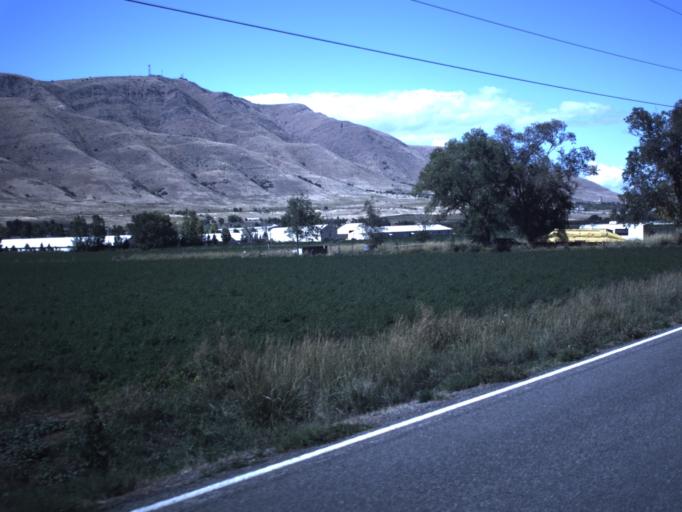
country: US
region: Utah
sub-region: Utah County
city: West Mountain
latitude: 40.0664
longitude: -111.7876
